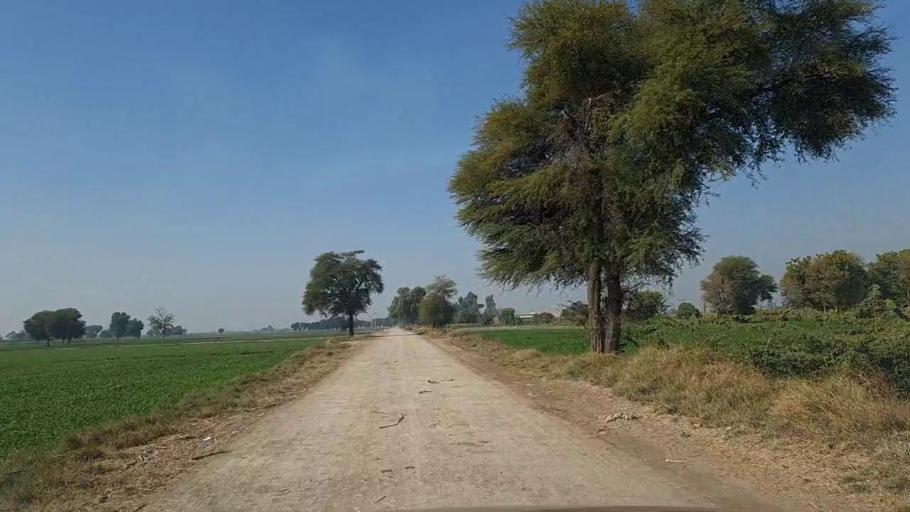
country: PK
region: Sindh
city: Nawabshah
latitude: 26.2823
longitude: 68.3840
